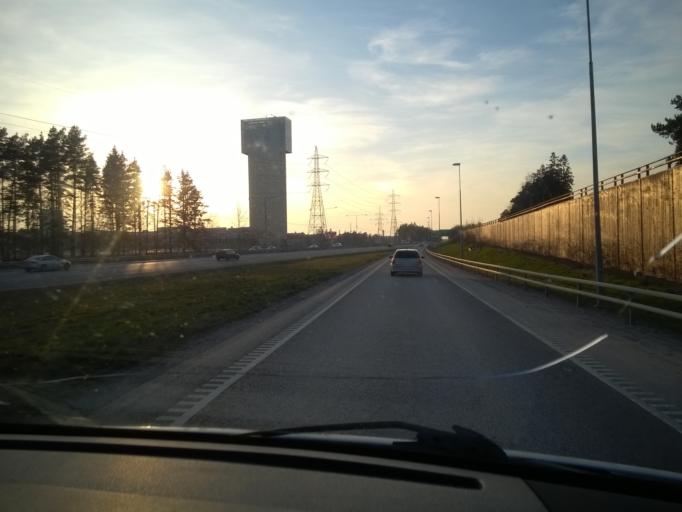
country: SE
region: Stockholm
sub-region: Stockholms Kommun
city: Kista
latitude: 59.4060
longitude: 17.9651
